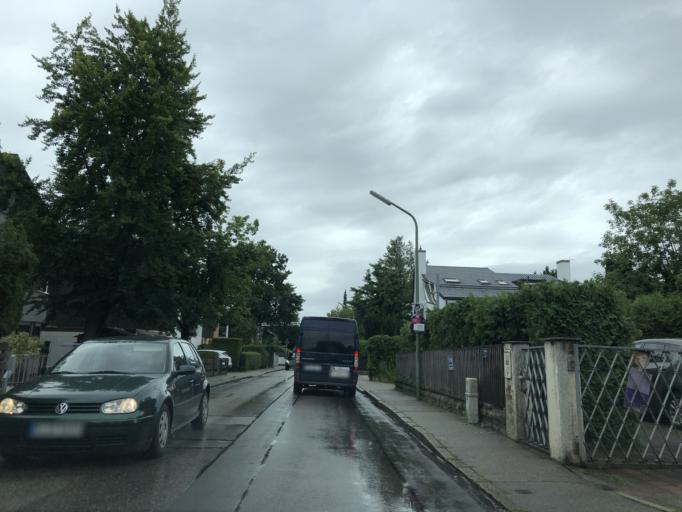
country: DE
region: Bavaria
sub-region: Upper Bavaria
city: Neubiberg
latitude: 48.1106
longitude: 11.6653
